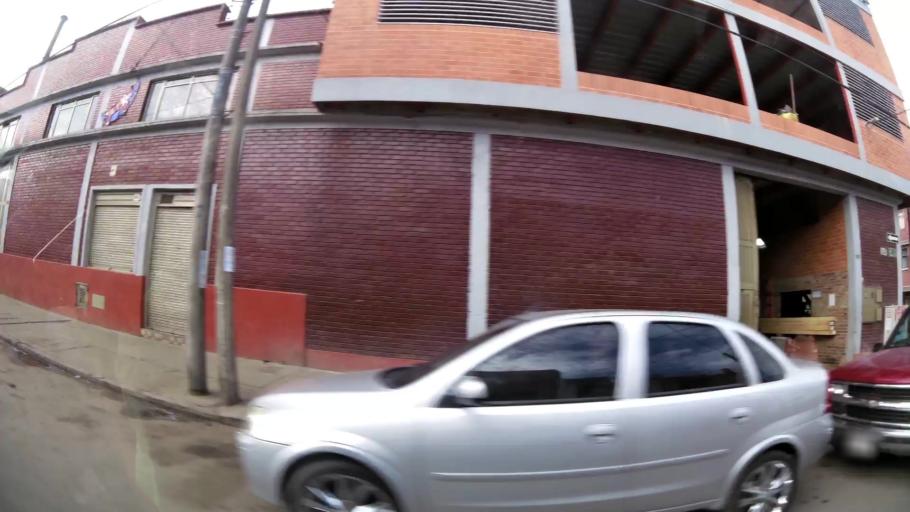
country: CO
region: Bogota D.C.
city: Bogota
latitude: 4.6324
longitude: -74.1100
